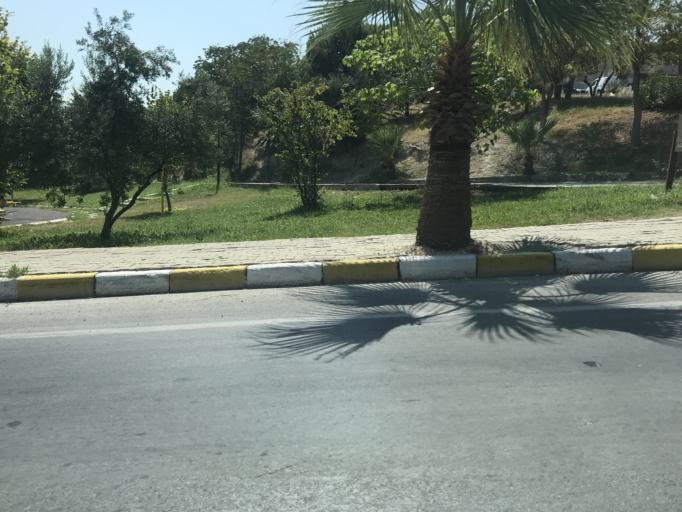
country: TR
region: Izmir
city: Urla
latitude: 38.3275
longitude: 26.7581
